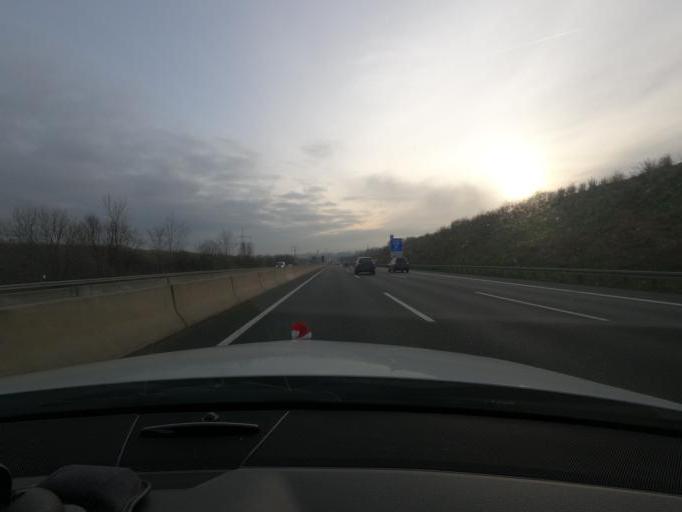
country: DE
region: Lower Saxony
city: Rosdorf
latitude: 51.5448
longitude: 9.8791
